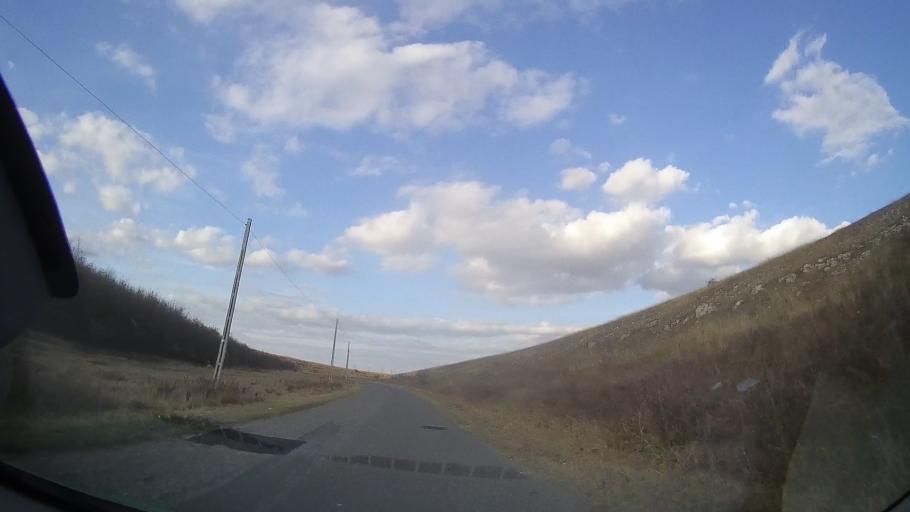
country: RO
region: Constanta
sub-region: Comuna Cerchezu
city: Cerchezu
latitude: 43.8354
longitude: 28.0975
